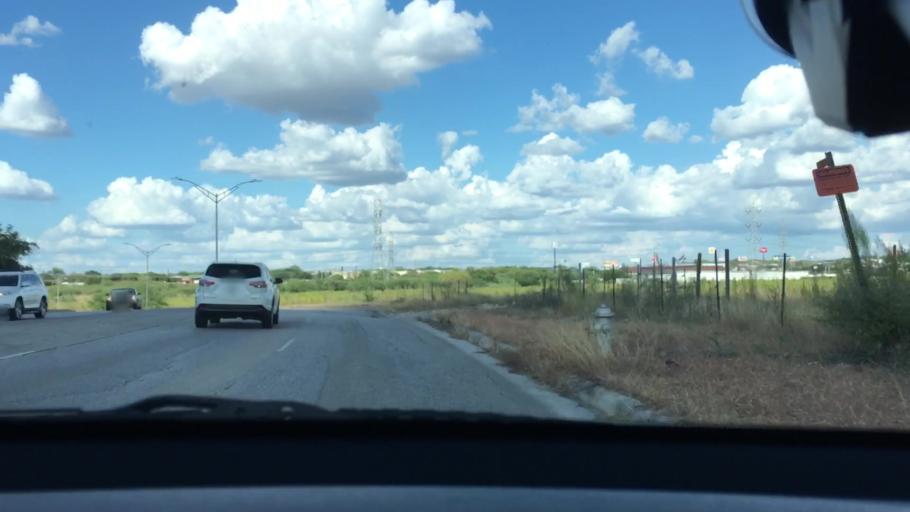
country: US
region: Texas
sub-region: Bexar County
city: Windcrest
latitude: 29.5447
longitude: -98.3762
